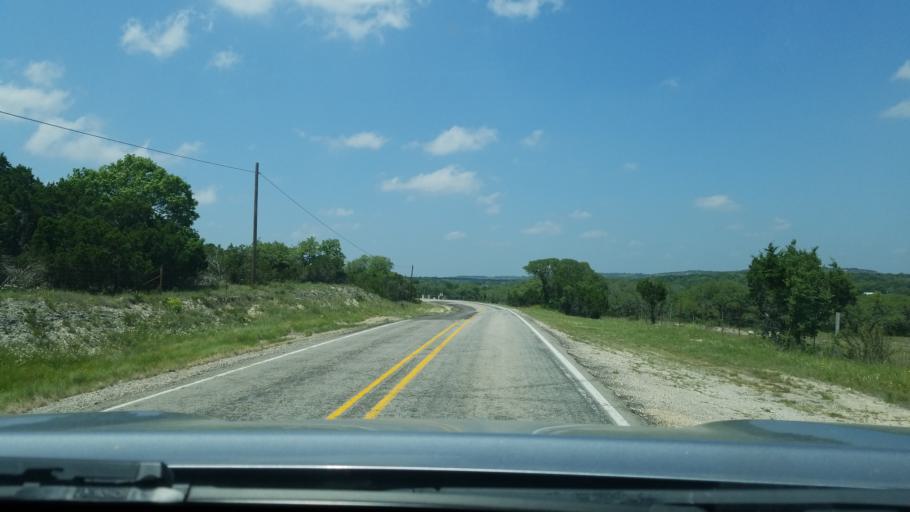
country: US
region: Texas
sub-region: Hays County
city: Woodcreek
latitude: 30.0750
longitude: -98.2213
